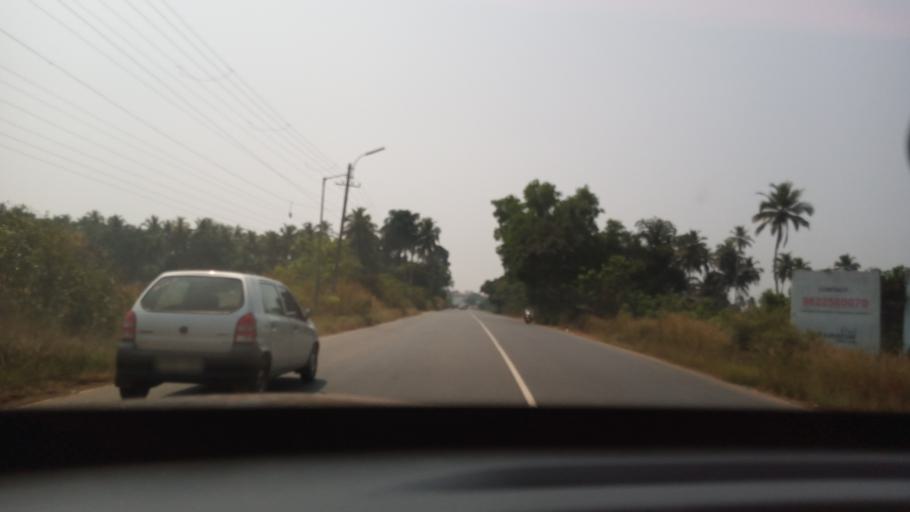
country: IN
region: Goa
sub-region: South Goa
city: Sancoale
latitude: 15.3399
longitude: 73.9279
